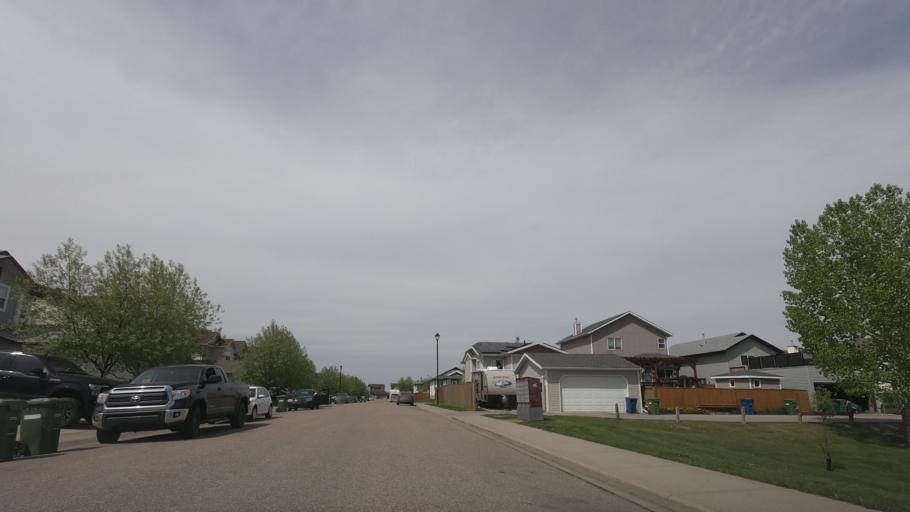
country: CA
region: Alberta
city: Airdrie
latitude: 51.3048
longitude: -114.0244
